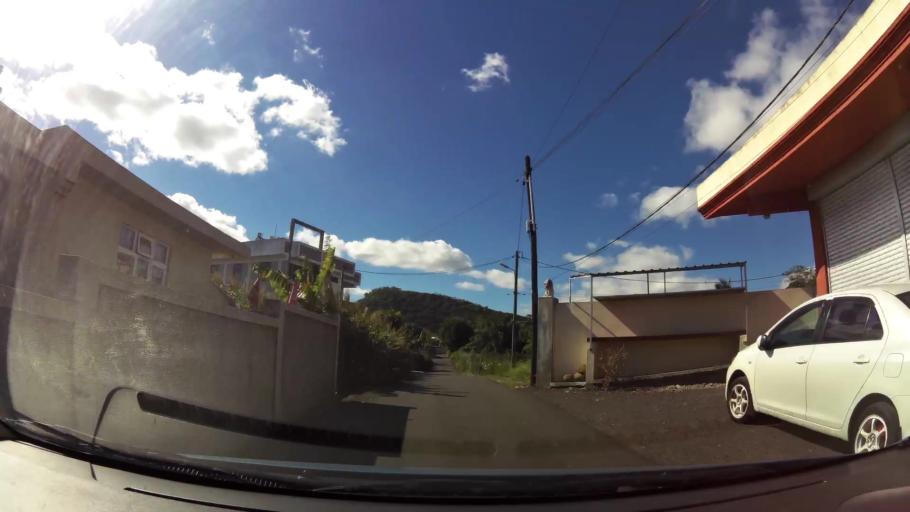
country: MU
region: Plaines Wilhems
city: Vacoas
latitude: -20.2831
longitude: 57.4773
